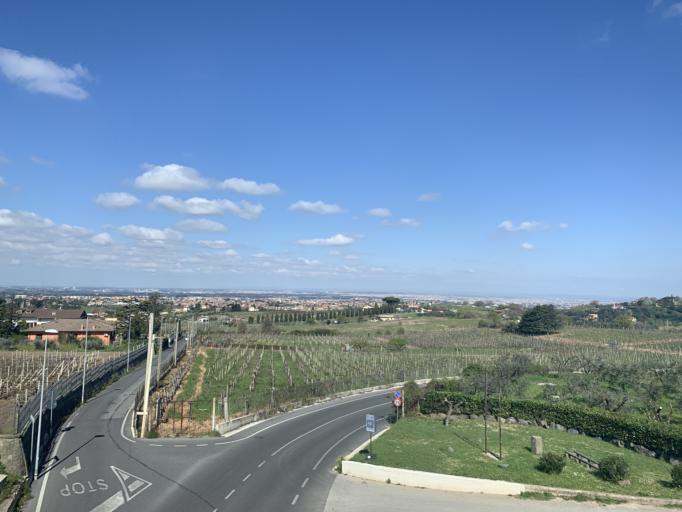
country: IT
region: Latium
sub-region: Citta metropolitana di Roma Capitale
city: Marino
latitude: 41.7843
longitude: 12.6440
